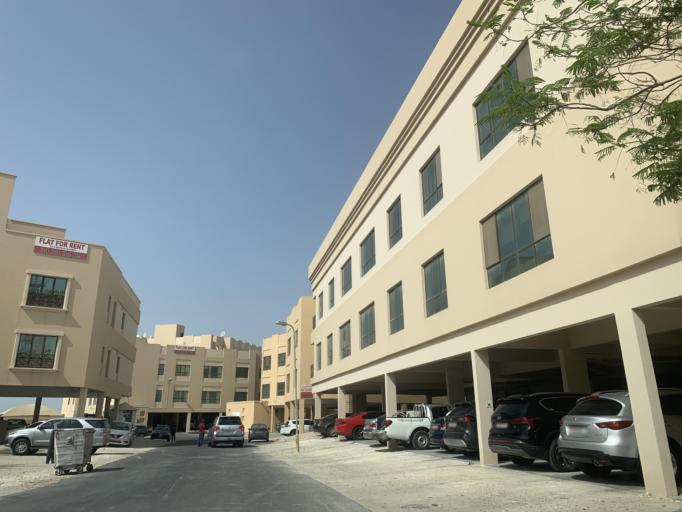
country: BH
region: Northern
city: Ar Rifa'
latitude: 26.1424
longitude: 50.5730
